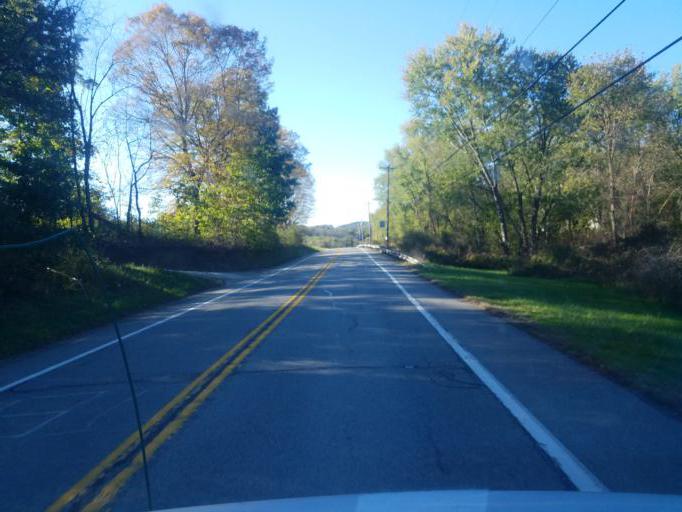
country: US
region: Pennsylvania
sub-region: Beaver County
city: Midland
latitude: 40.5816
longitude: -80.4891
